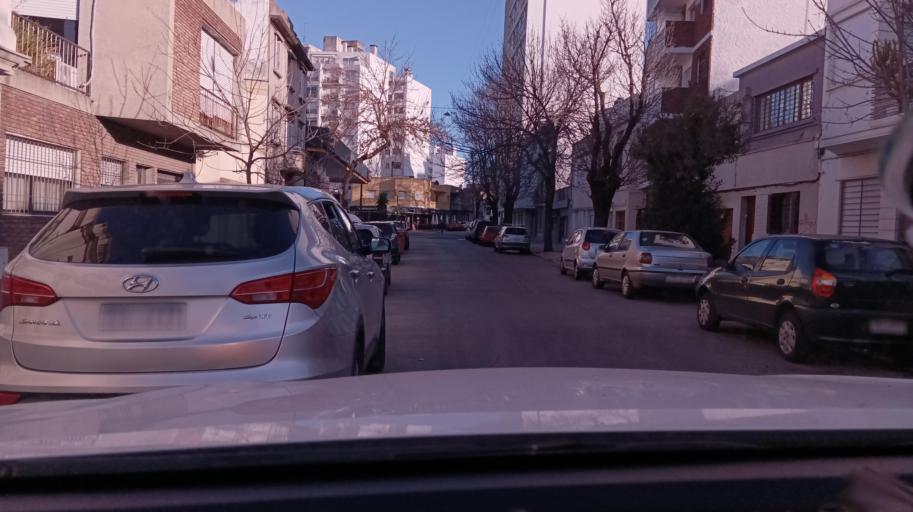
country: UY
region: Montevideo
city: Montevideo
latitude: -34.9065
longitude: -56.1583
